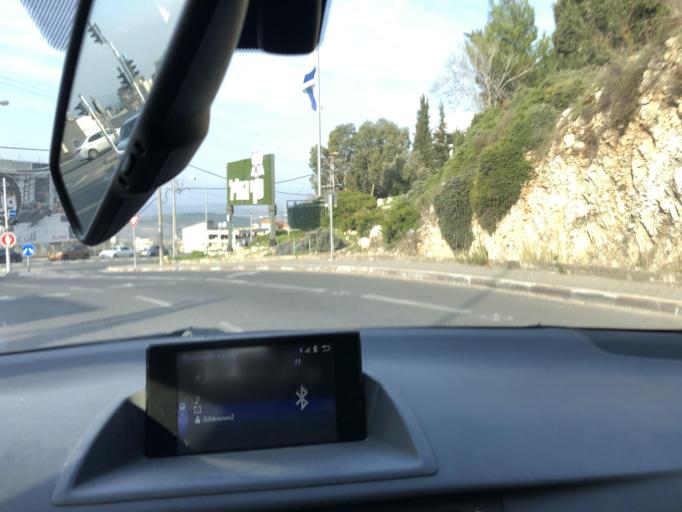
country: IL
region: Northern District
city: Nazareth
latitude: 32.7105
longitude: 35.3064
